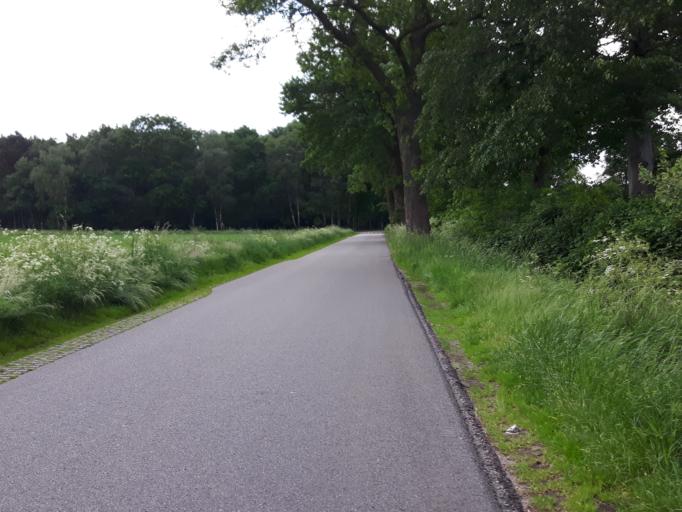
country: NL
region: Overijssel
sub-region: Gemeente Enschede
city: Enschede
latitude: 52.1681
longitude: 6.8565
